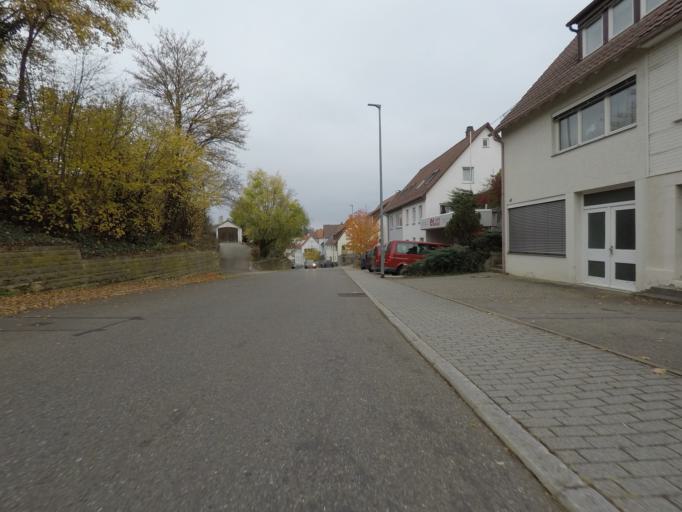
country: DE
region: Baden-Wuerttemberg
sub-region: Tuebingen Region
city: Reutlingen
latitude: 48.5182
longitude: 9.2323
